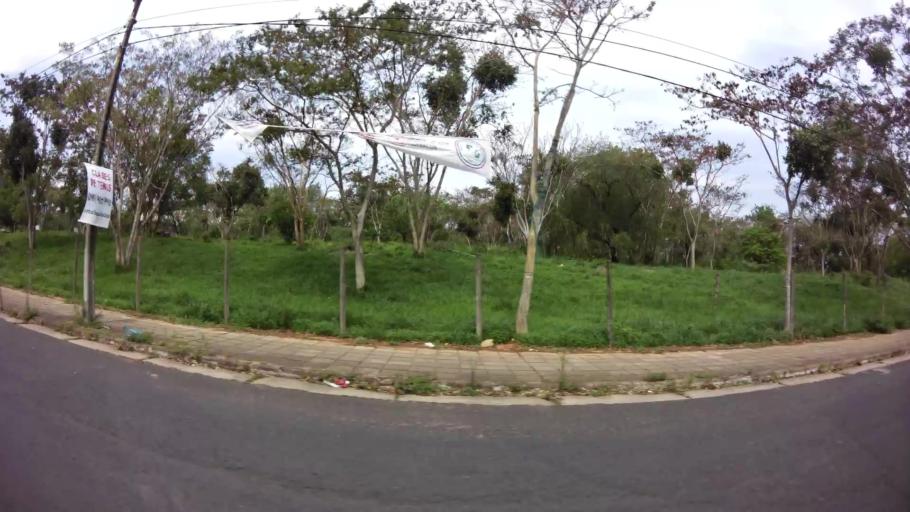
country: PY
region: Asuncion
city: Asuncion
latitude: -25.2783
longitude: -57.5786
